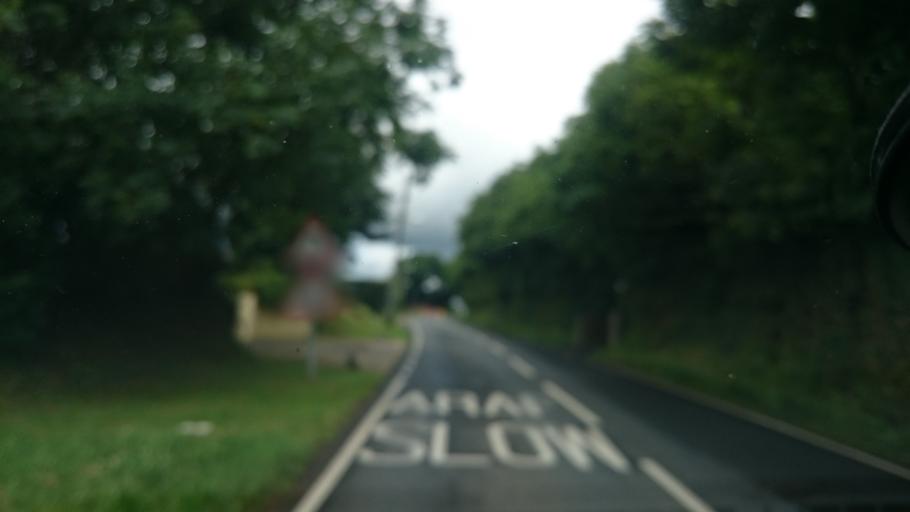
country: GB
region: Wales
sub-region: Pembrokeshire
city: Llangwm
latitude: 51.7335
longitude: -4.9212
